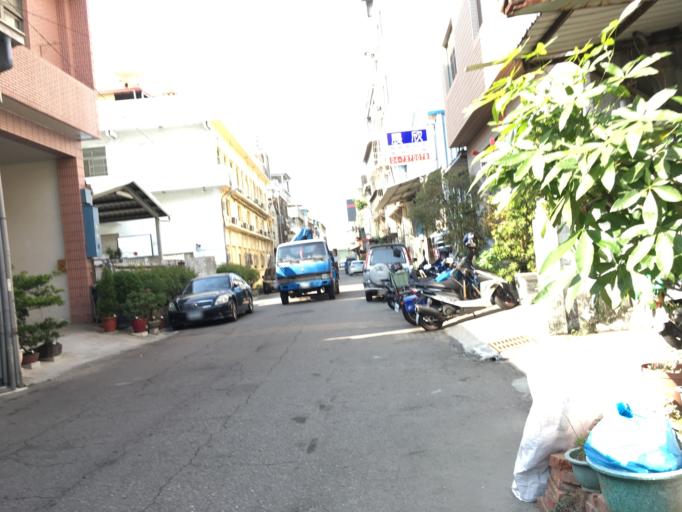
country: TW
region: Taiwan
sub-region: Changhua
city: Chang-hua
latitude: 24.0862
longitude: 120.5577
